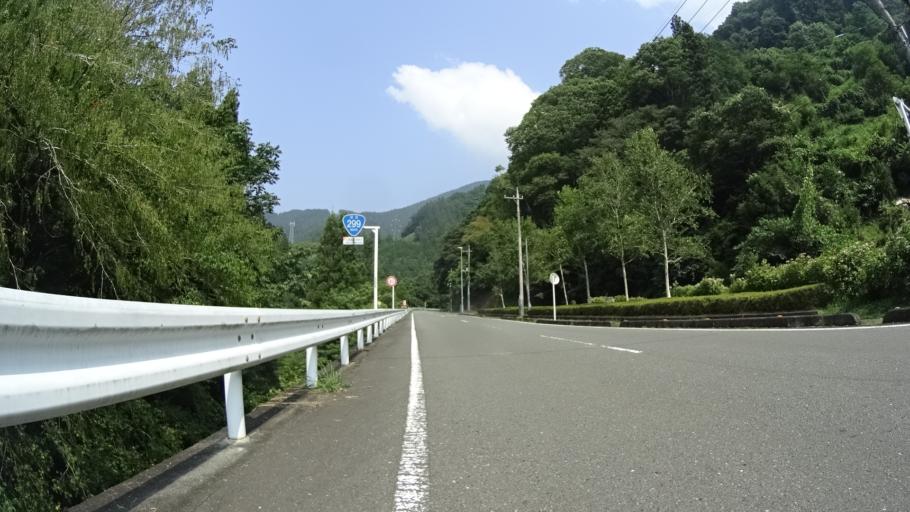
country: JP
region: Gunma
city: Tomioka
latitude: 36.0565
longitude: 138.8586
